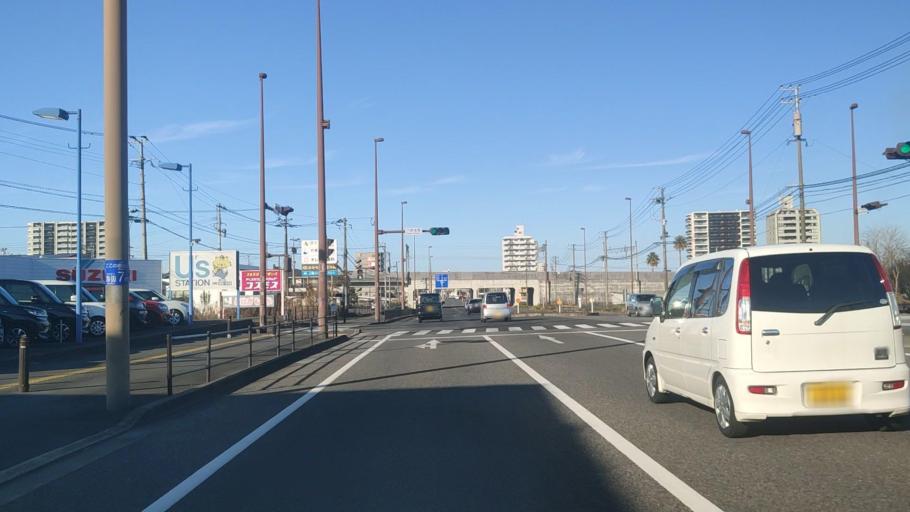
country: JP
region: Oita
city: Oita
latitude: 33.2272
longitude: 131.6188
